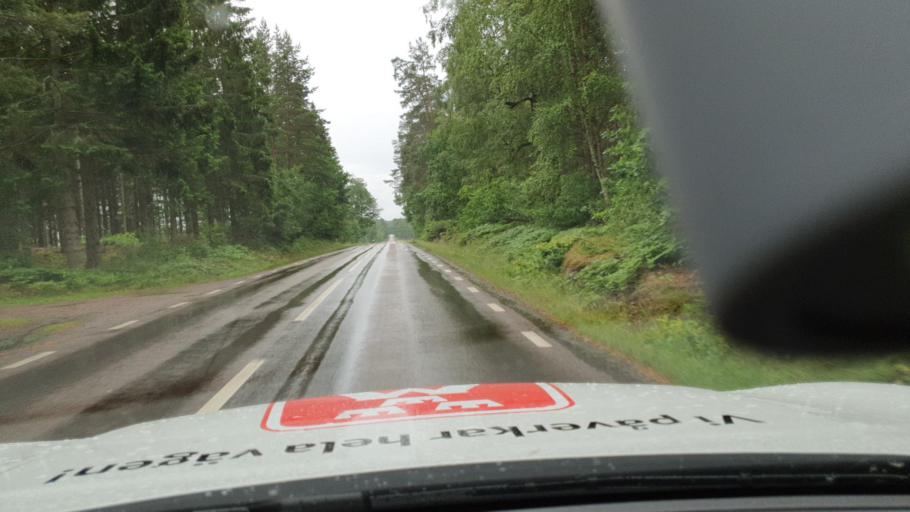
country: SE
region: Vaestra Goetaland
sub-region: Mariestads Kommun
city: Mariestad
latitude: 58.7389
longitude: 13.8965
